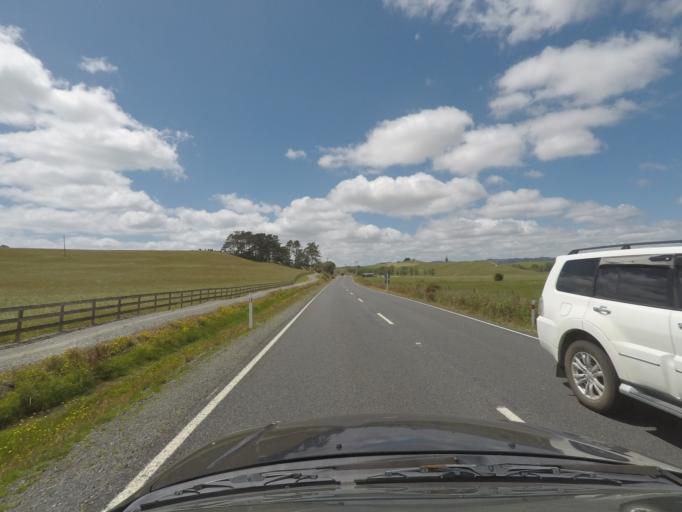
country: NZ
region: Northland
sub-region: Whangarei
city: Ruakaka
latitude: -35.9916
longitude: 174.4606
